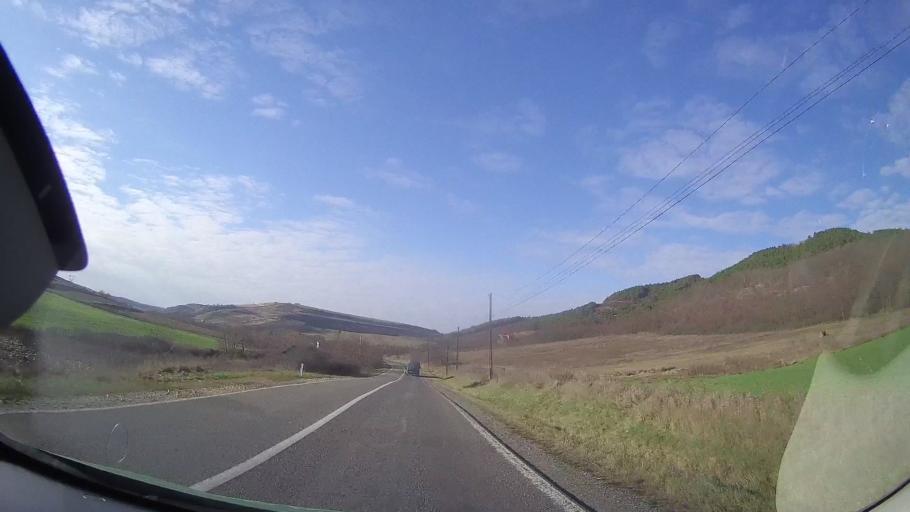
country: RO
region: Cluj
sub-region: Comuna Caianu
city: Caianu
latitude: 46.8009
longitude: 23.9391
